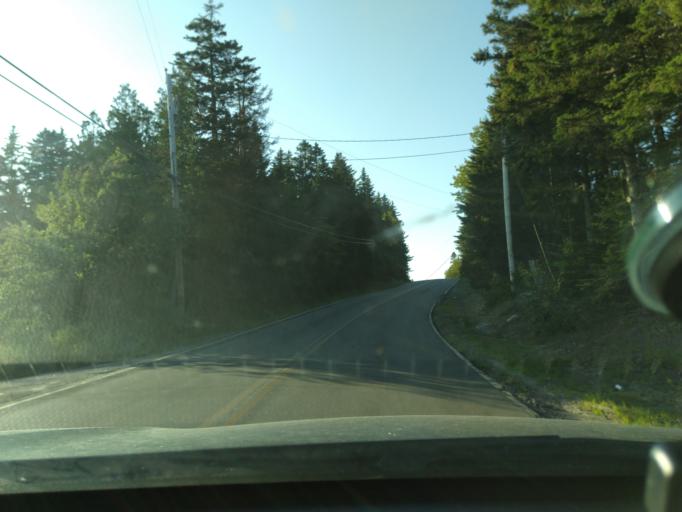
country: US
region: Maine
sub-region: Washington County
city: Machiasport
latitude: 44.6620
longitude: -67.2364
